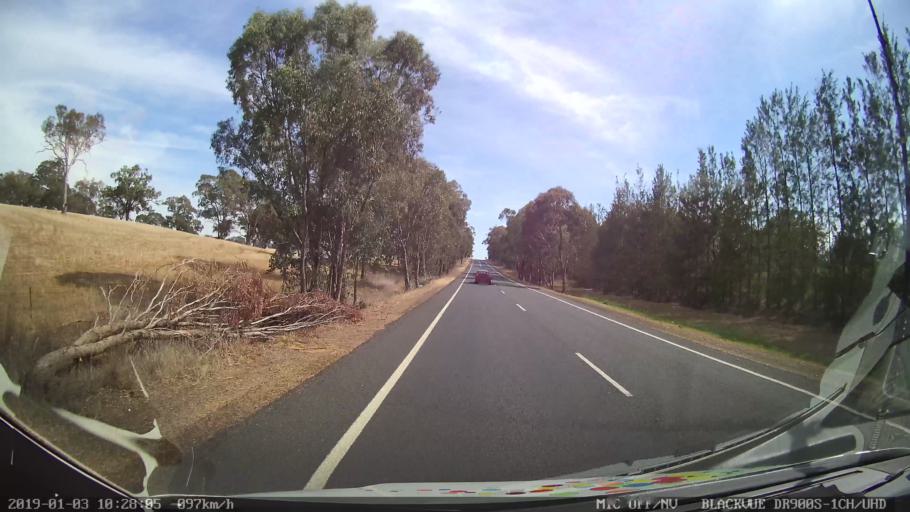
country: AU
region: New South Wales
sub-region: Young
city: Young
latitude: -34.3929
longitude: 148.2586
